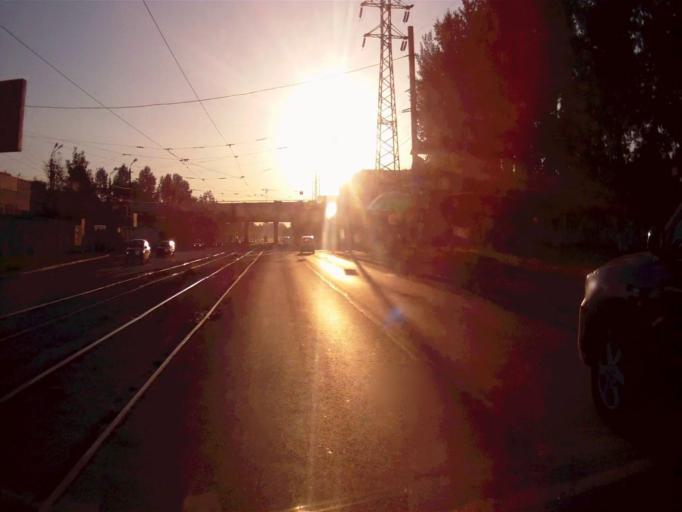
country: RU
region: Chelyabinsk
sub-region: Gorod Chelyabinsk
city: Chelyabinsk
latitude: 55.1683
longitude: 61.4307
